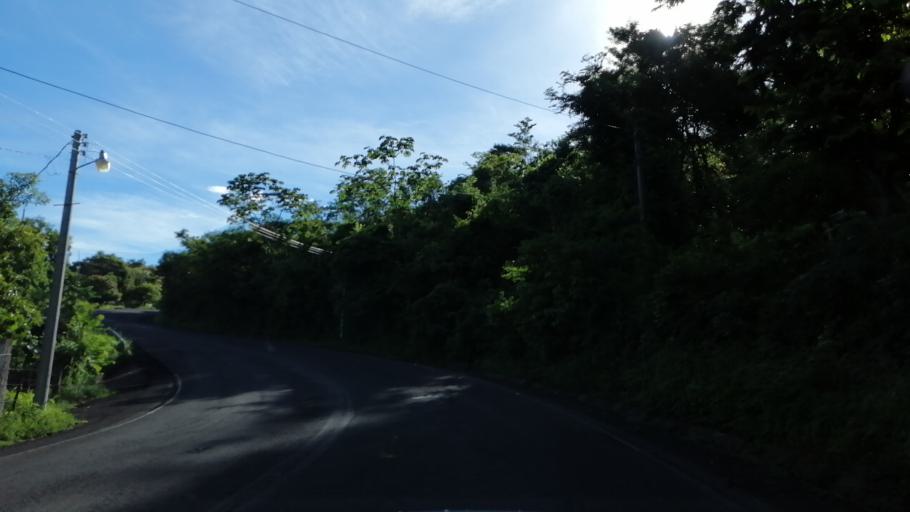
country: SV
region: Morazan
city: Cacaopera
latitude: 13.7916
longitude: -88.1246
